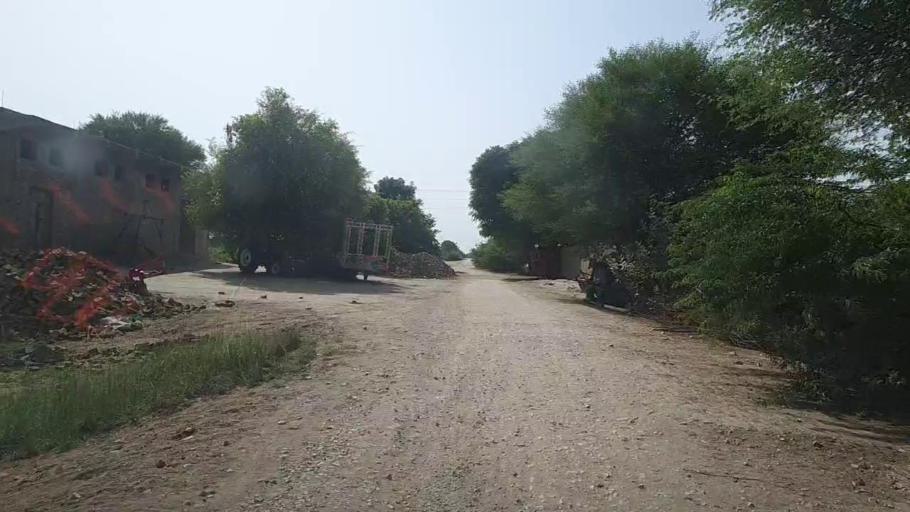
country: PK
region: Sindh
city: Pad Idan
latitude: 26.7648
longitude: 68.3275
